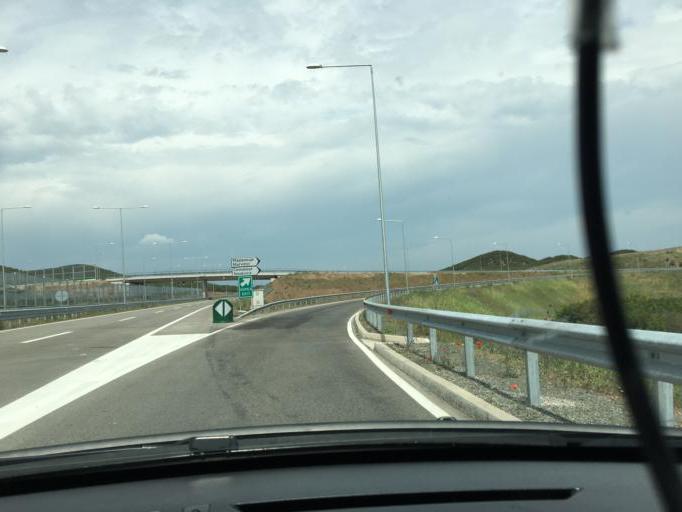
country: MK
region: Gevgelija
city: Miravci
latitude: 41.2609
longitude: 22.4727
